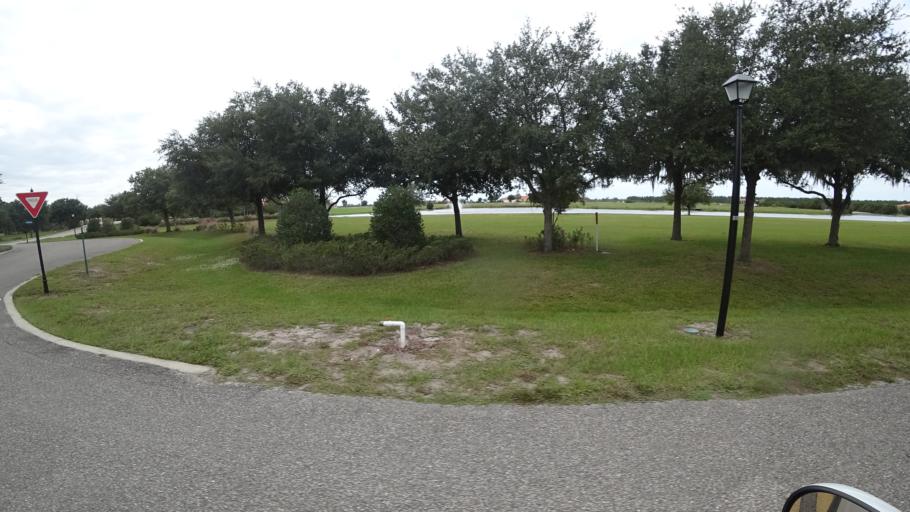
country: US
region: Florida
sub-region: Hillsborough County
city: Wimauma
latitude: 27.6549
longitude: -82.3255
